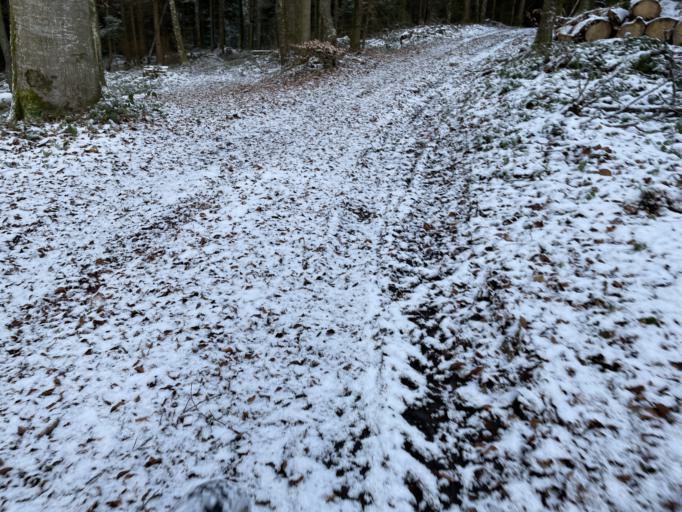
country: CH
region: Lucerne
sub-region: Entlebuch District
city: Oberdiessbach
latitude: 46.8549
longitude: 7.6117
